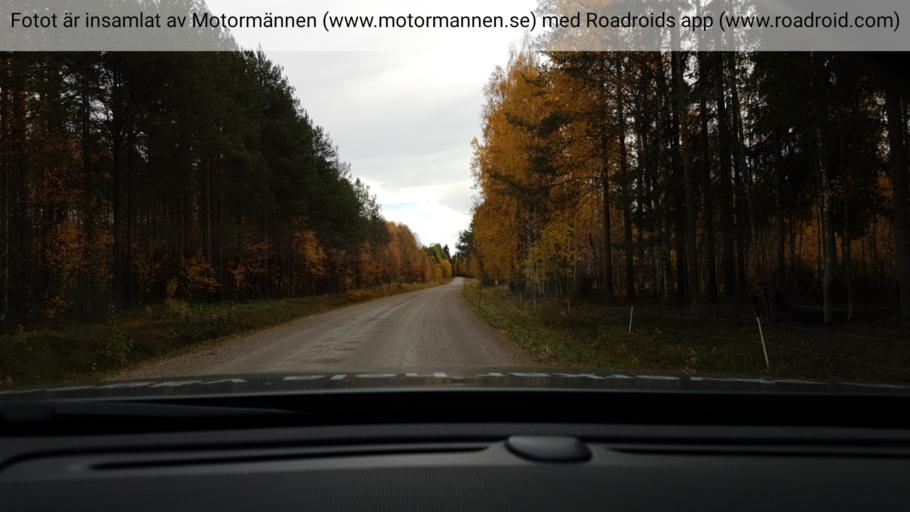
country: SE
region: Norrbotten
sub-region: Overkalix Kommun
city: OEverkalix
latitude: 66.3010
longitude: 22.9340
